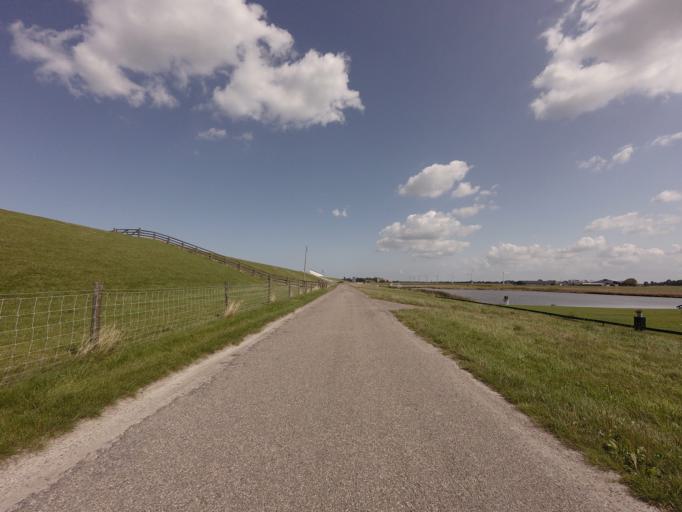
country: NL
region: Friesland
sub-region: Gemeente Ferwerderadiel
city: Hallum
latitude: 53.3200
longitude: 5.7570
